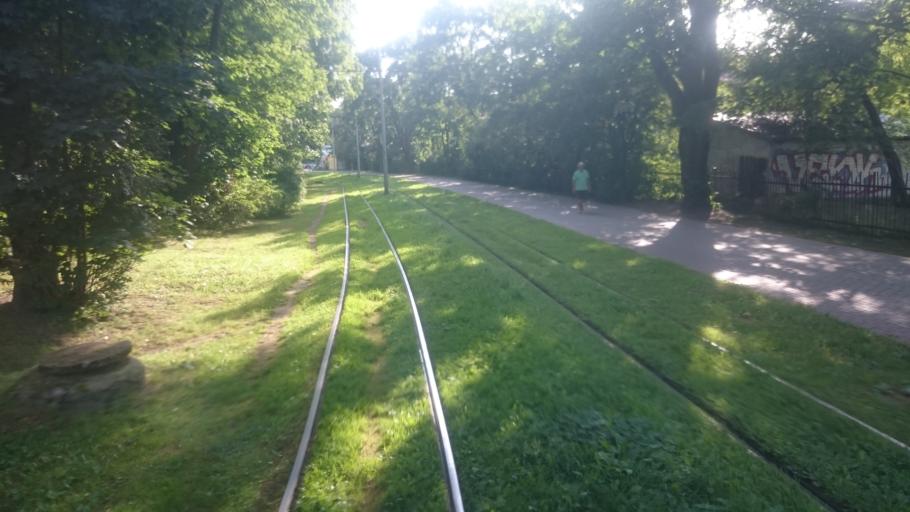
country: RU
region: Kaliningrad
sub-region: Gorod Kaliningrad
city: Kaliningrad
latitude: 54.7240
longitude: 20.4614
